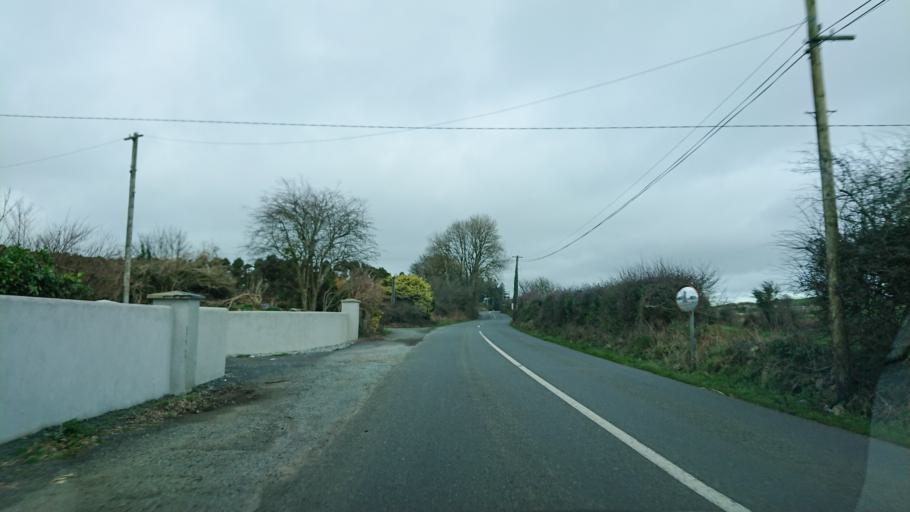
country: IE
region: Leinster
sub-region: Kilkenny
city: Mooncoin
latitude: 52.1953
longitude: -7.2724
